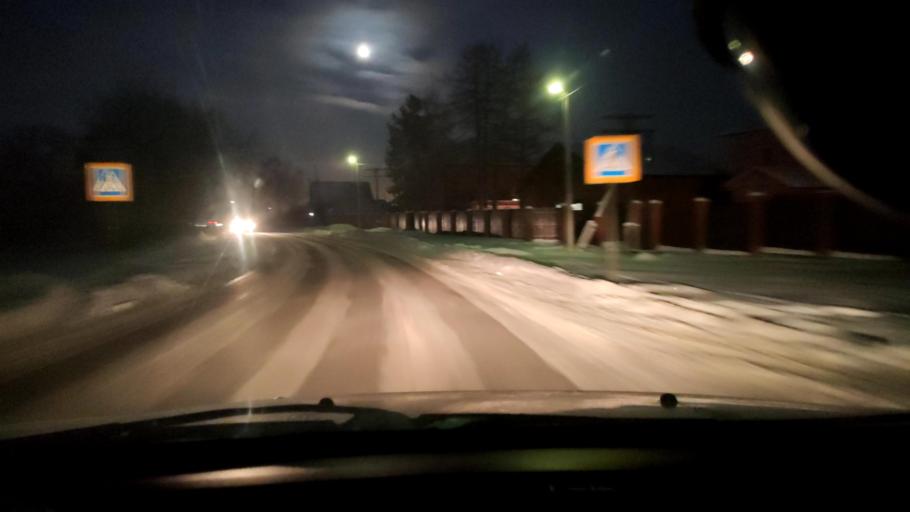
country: RU
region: Perm
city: Kultayevo
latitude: 57.8948
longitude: 55.9449
